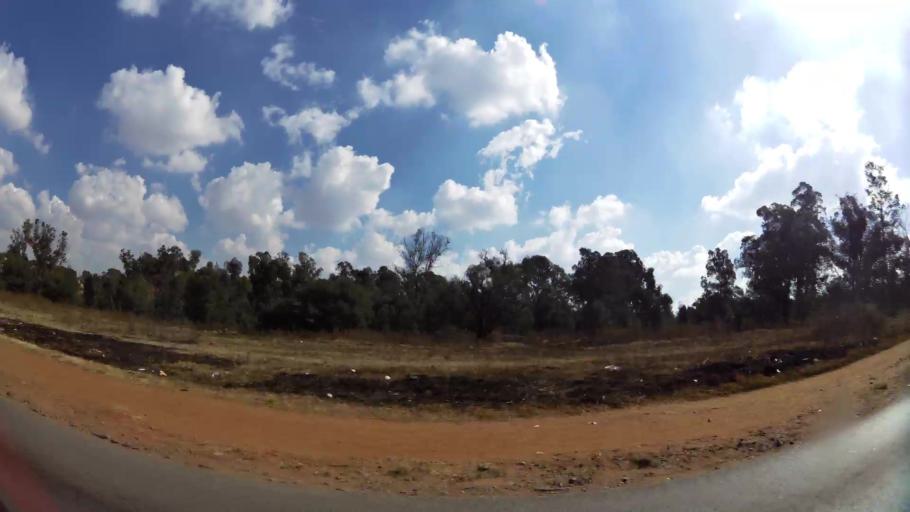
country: ZA
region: Gauteng
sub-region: City of Johannesburg Metropolitan Municipality
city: Roodepoort
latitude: -26.1786
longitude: 27.8708
